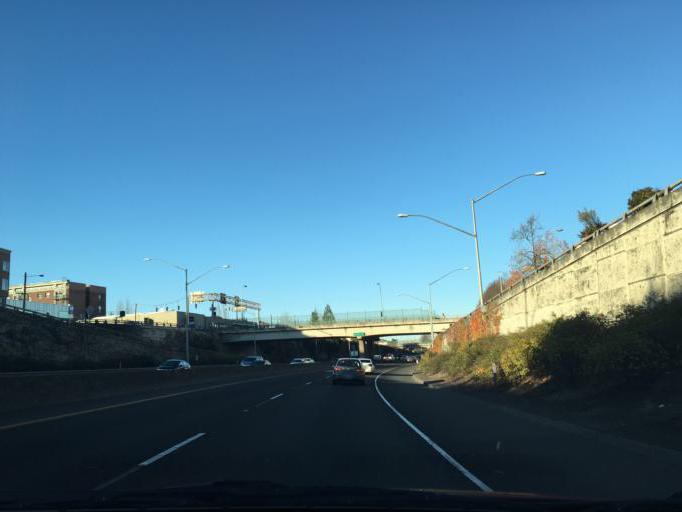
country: US
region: Oregon
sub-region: Multnomah County
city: Portland
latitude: 45.5239
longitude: -122.6863
